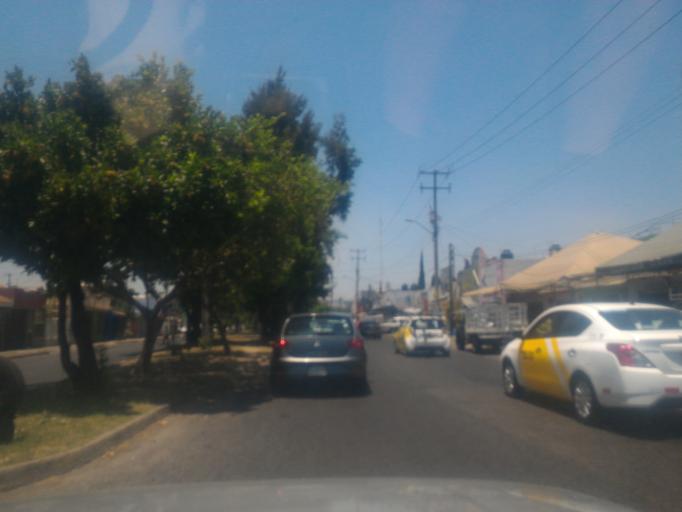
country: MX
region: Jalisco
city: Tlaquepaque
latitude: 20.6655
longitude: -103.2979
